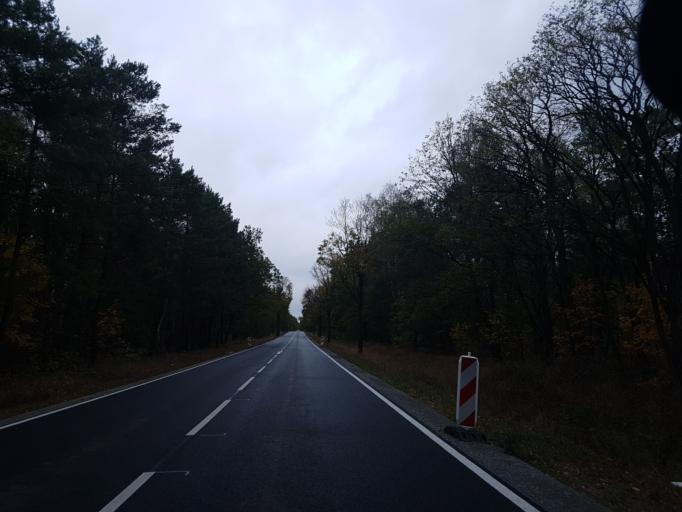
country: DE
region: Brandenburg
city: Treuenbrietzen
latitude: 52.0667
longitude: 12.8296
